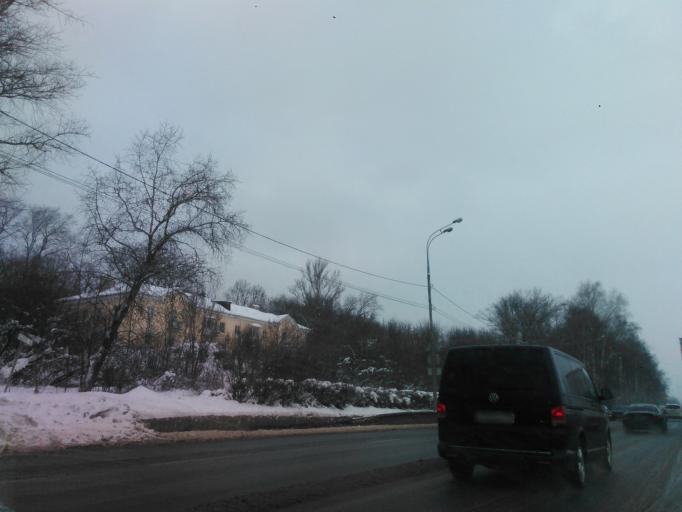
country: RU
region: Moskovskaya
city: Iksha
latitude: 56.1654
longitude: 37.5024
